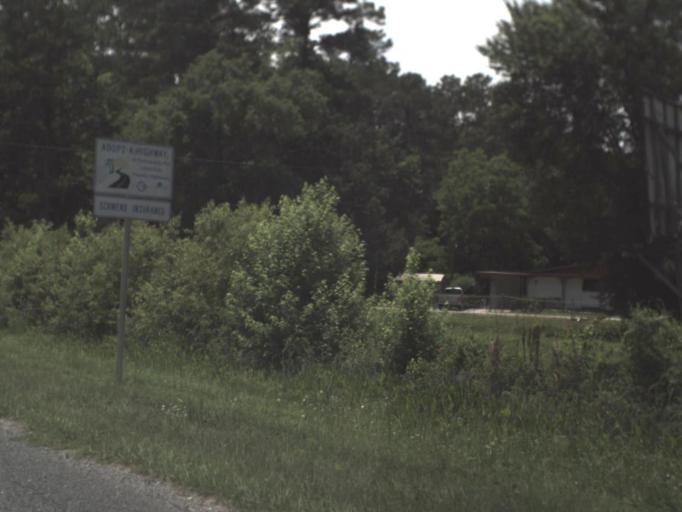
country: US
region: Florida
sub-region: Nassau County
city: Callahan
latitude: 30.5561
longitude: -81.8241
